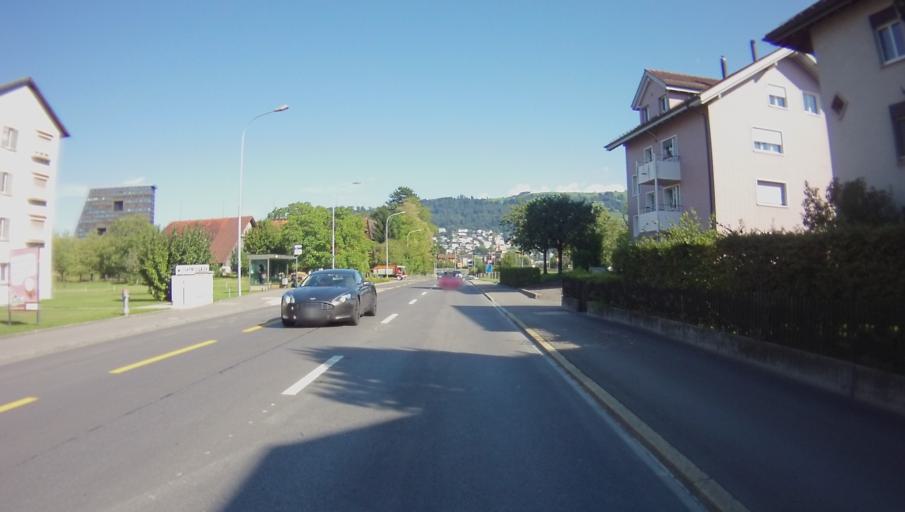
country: CH
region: Zug
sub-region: Zug
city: Zug
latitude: 47.1763
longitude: 8.5008
